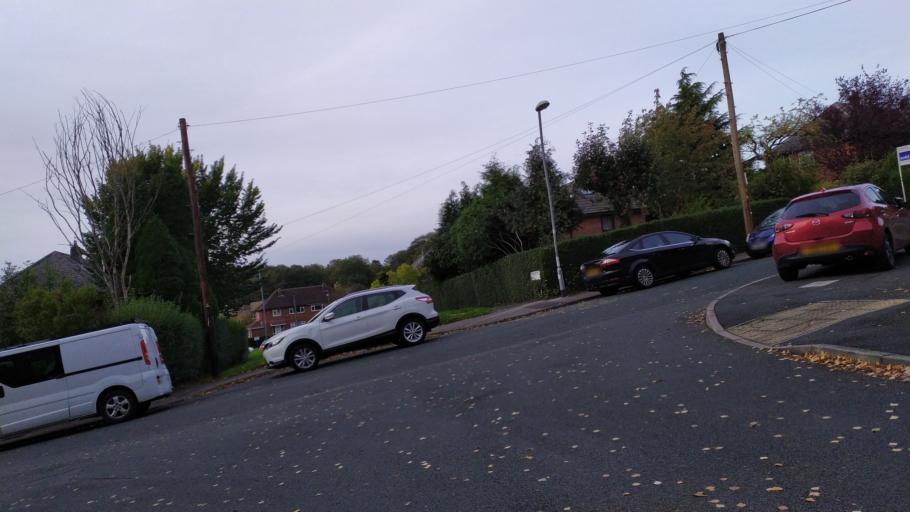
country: GB
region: England
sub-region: City and Borough of Leeds
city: Leeds
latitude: 53.8212
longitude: -1.5914
